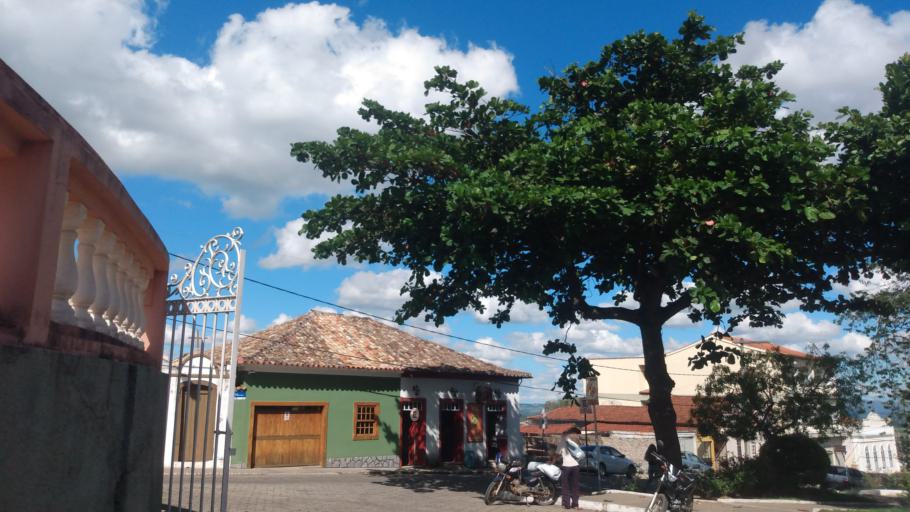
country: BR
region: Minas Gerais
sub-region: Tiradentes
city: Tiradentes
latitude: -20.9231
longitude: -44.2380
